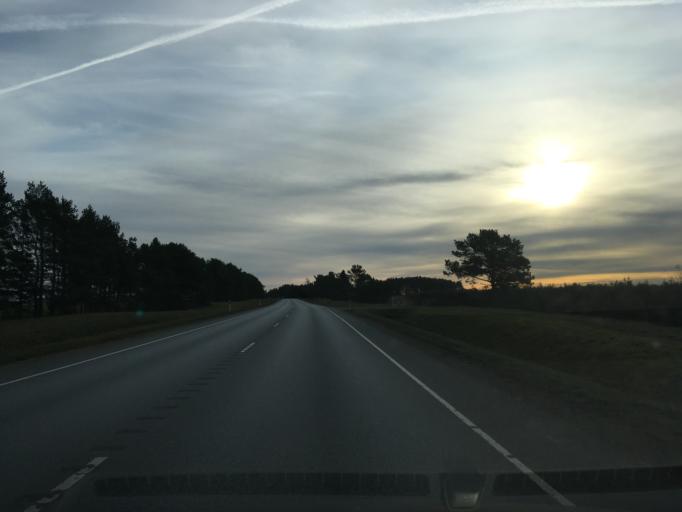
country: EE
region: Ida-Virumaa
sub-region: Puessi linn
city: Pussi
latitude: 59.4088
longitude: 27.0517
